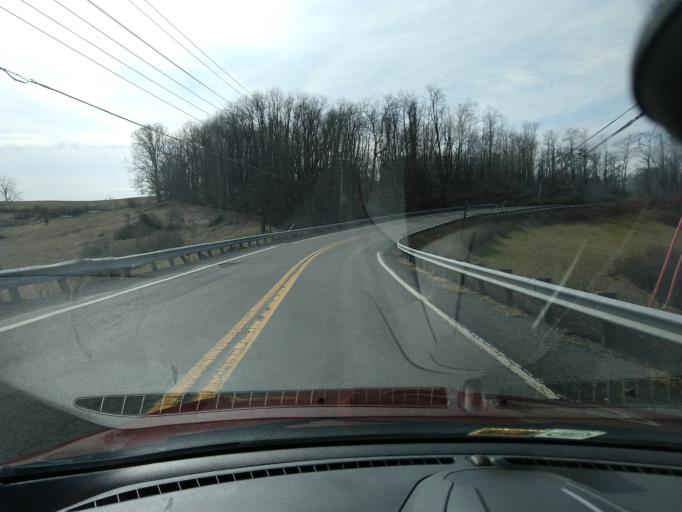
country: US
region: West Virginia
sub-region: Greenbrier County
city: Lewisburg
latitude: 37.8767
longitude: -80.4113
